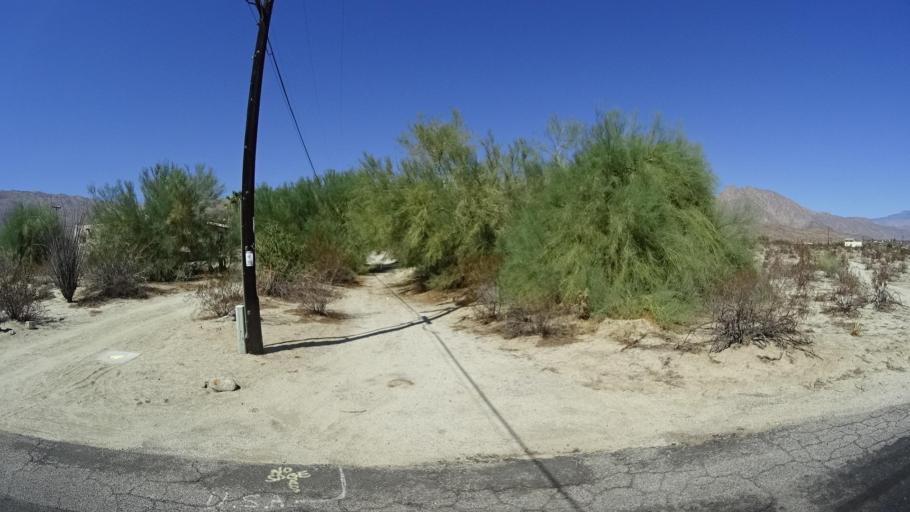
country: US
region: California
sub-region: San Diego County
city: Borrego Springs
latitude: 33.2344
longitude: -116.3722
